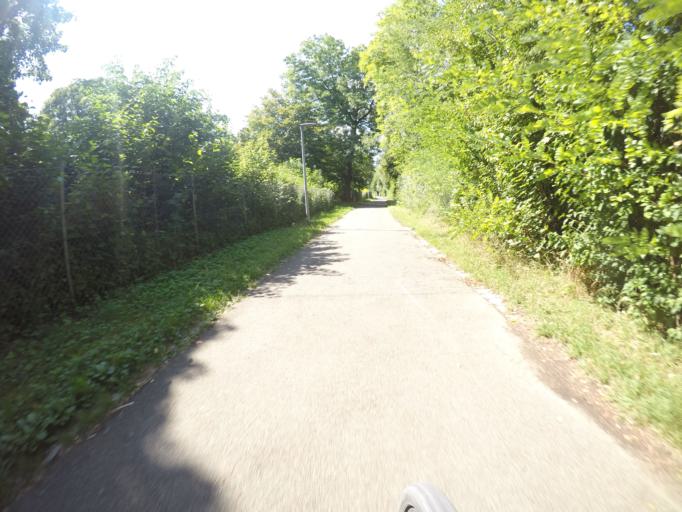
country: DE
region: Baden-Wuerttemberg
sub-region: Regierungsbezirk Stuttgart
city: Esslingen
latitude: 48.7262
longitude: 9.3288
